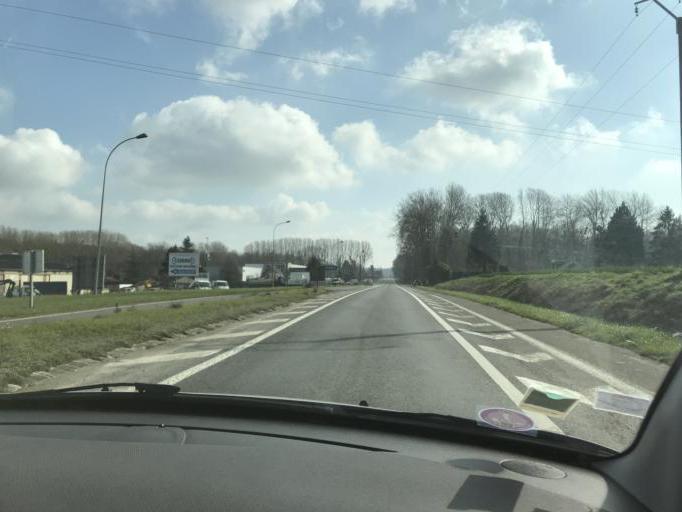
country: FR
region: Picardie
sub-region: Departement de l'Aisne
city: Villeneuve-Saint-Germain
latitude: 49.3676
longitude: 3.3673
